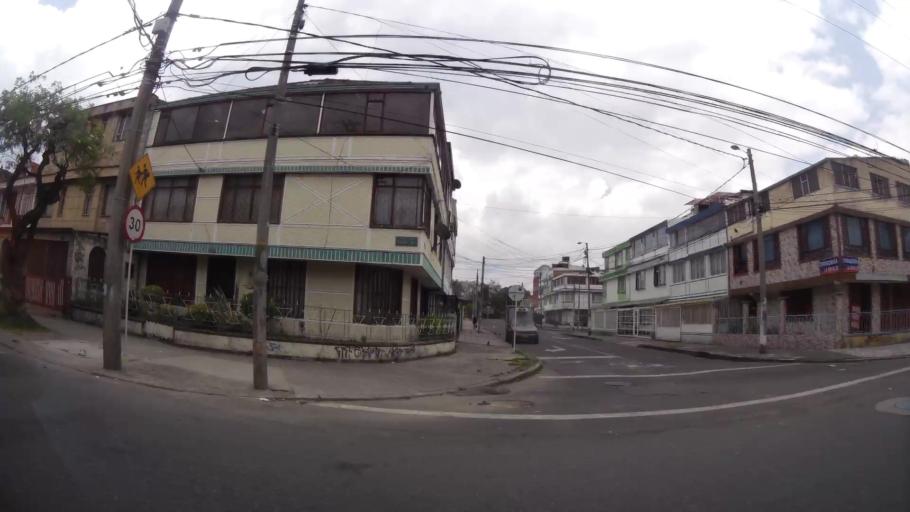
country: CO
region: Bogota D.C.
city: Bogota
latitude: 4.5972
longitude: -74.1056
